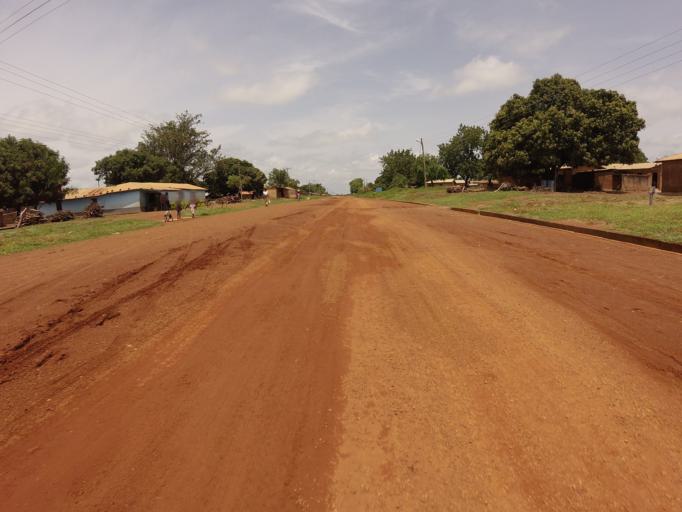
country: GH
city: Kpandae
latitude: 8.5891
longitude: 0.2378
